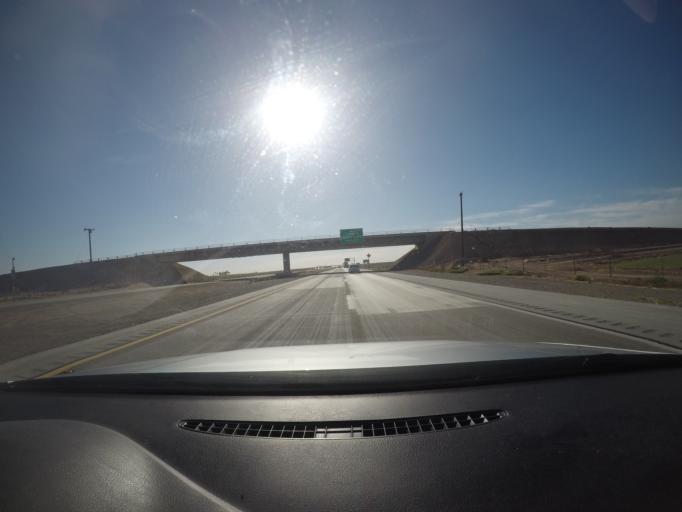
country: US
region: California
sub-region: Imperial County
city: Holtville
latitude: 32.7732
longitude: -115.3971
